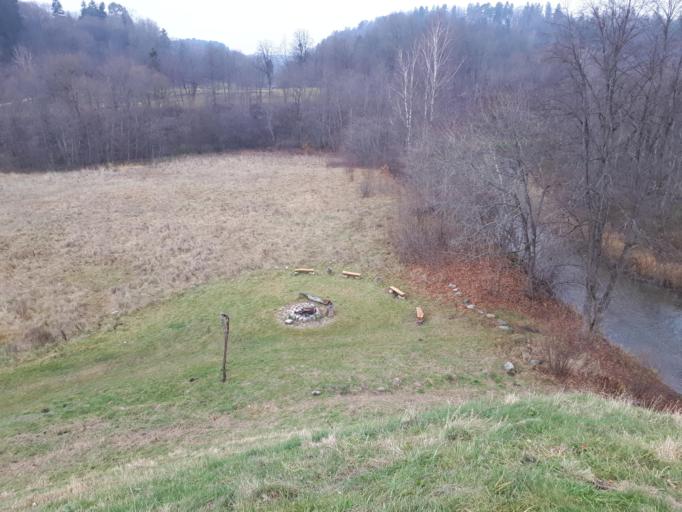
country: LT
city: Birstonas
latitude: 54.6069
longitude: 24.0853
